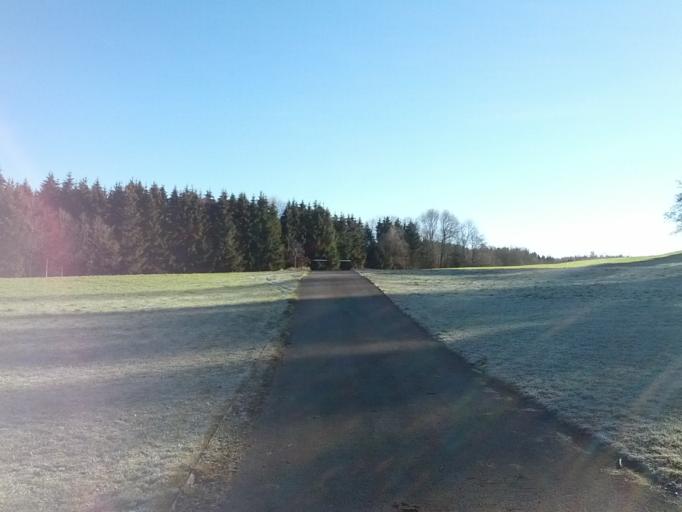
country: DE
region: Baden-Wuerttemberg
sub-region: Tuebingen Region
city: Steinhausen an der Rottum
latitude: 47.9851
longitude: 9.9920
